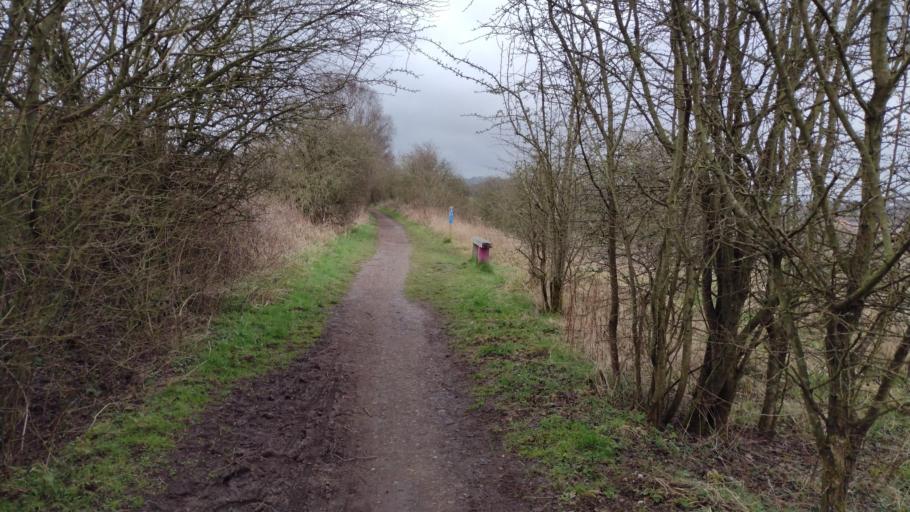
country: GB
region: England
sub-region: Wiltshire
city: Marlborough
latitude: 51.4335
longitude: -1.7267
